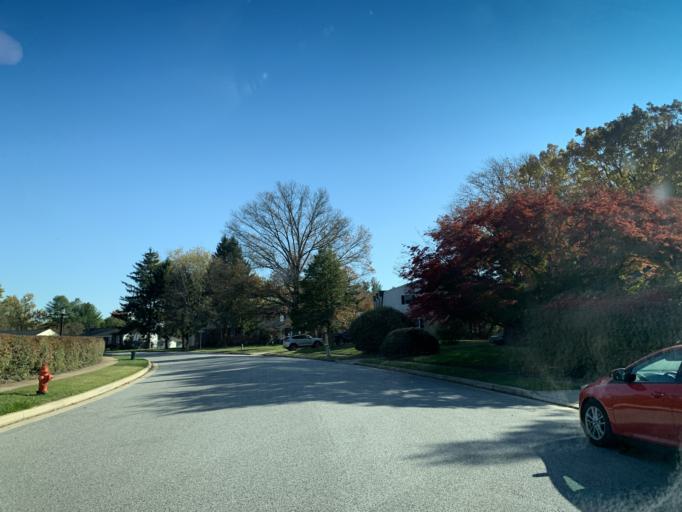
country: US
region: Maryland
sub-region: Baltimore County
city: Timonium
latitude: 39.4534
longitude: -76.6263
